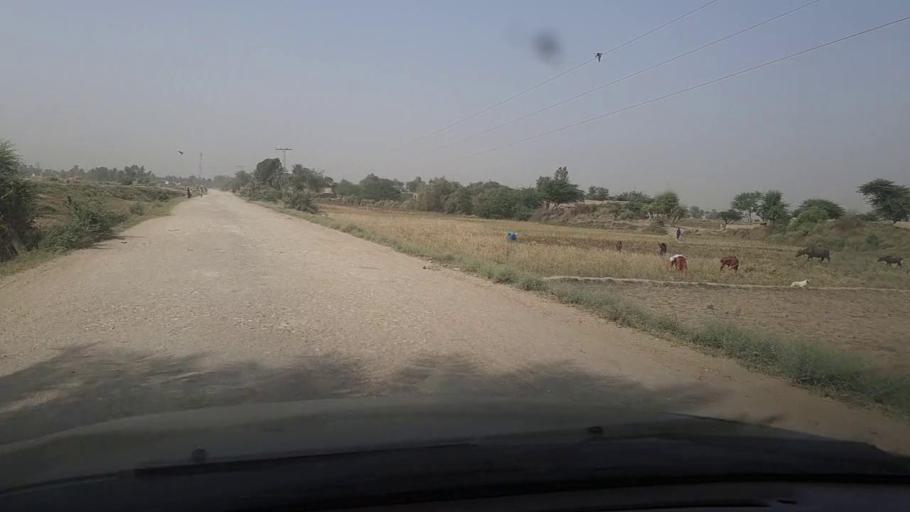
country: PK
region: Sindh
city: Garhi Yasin
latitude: 27.8683
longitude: 68.5557
